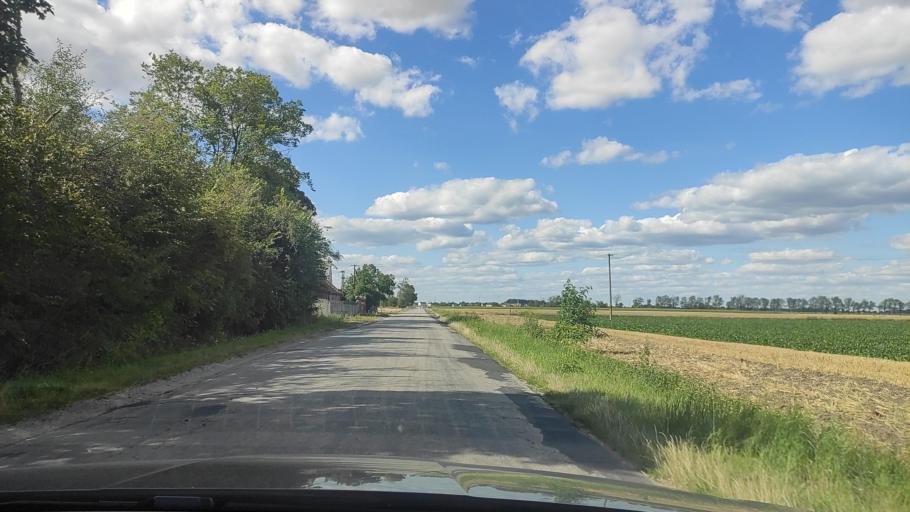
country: PL
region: Greater Poland Voivodeship
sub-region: Powiat poznanski
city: Kleszczewo
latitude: 52.3621
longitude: 17.1695
